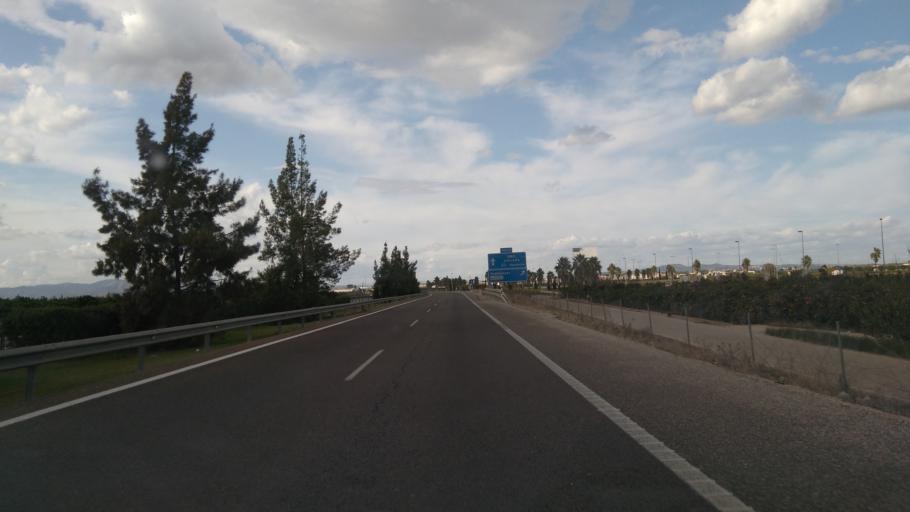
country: ES
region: Valencia
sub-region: Provincia de Valencia
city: Guadassuar
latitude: 39.1721
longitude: -0.4654
